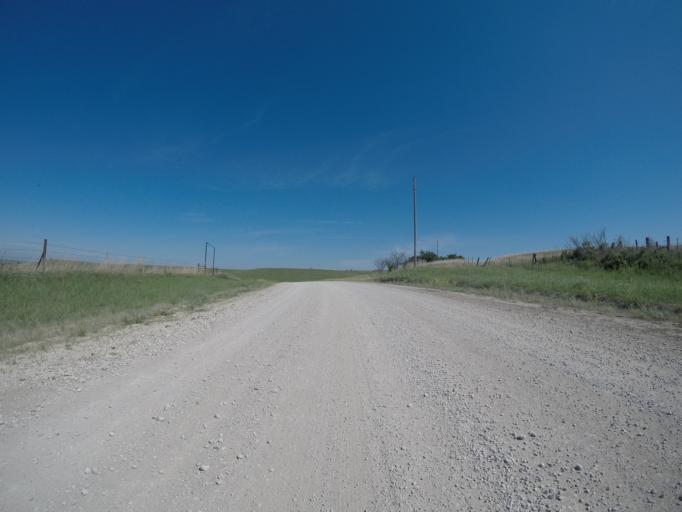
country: US
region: Kansas
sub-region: Wabaunsee County
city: Alma
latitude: 39.0145
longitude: -96.1138
